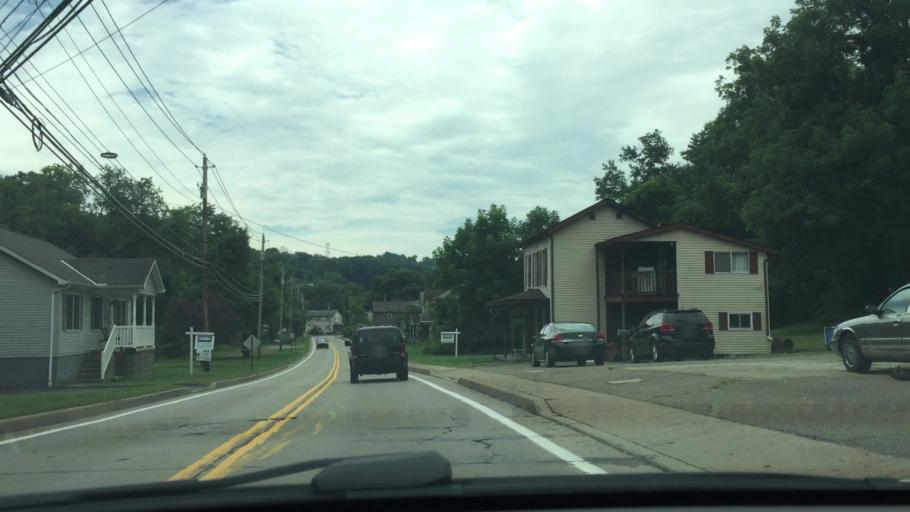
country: US
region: Pennsylvania
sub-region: Allegheny County
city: Oakdale
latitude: 40.4015
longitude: -80.1884
